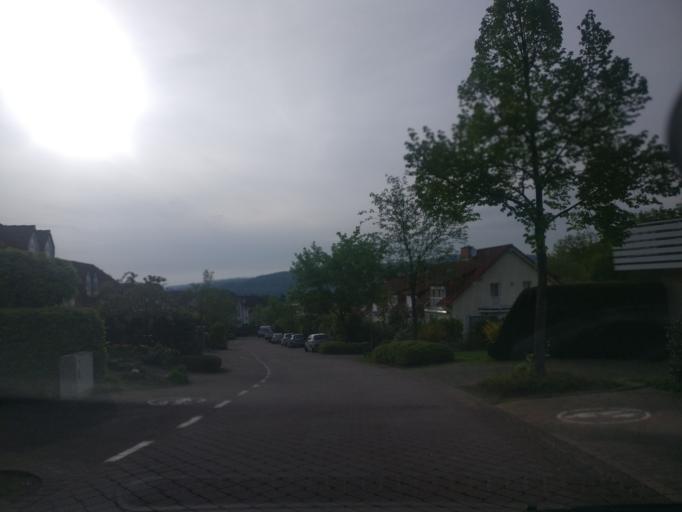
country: DE
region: Lower Saxony
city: Hannoversch Munden
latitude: 51.4016
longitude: 9.6659
